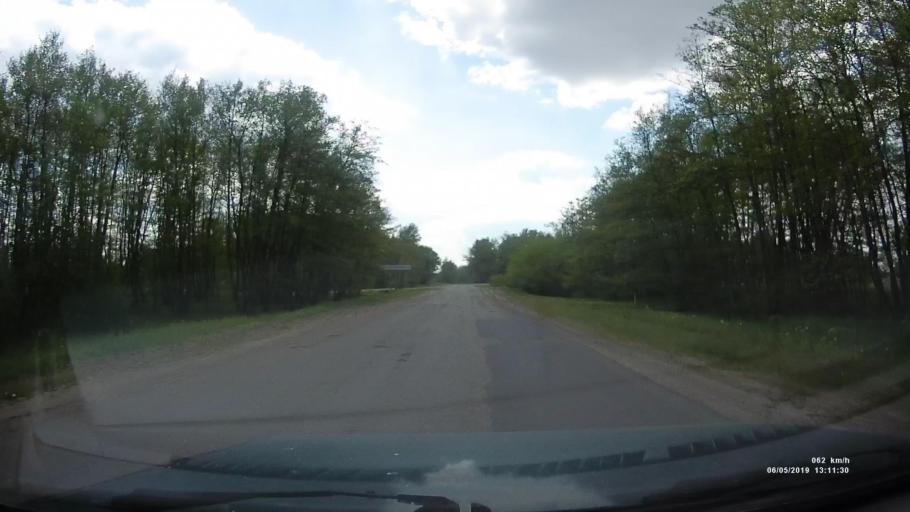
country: RU
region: Rostov
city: Ust'-Donetskiy
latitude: 47.7550
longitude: 40.9577
